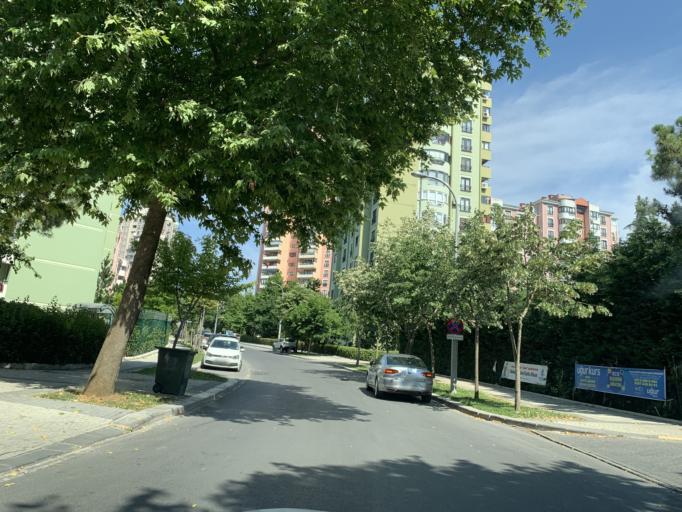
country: TR
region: Istanbul
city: Esenyurt
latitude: 41.0664
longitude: 28.6785
